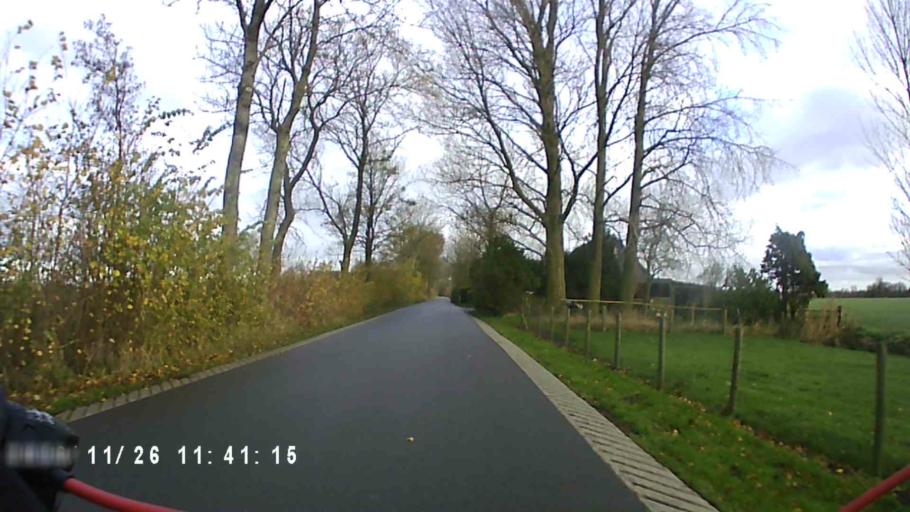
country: NL
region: Groningen
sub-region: Gemeente Bedum
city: Bedum
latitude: 53.2902
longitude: 6.5717
